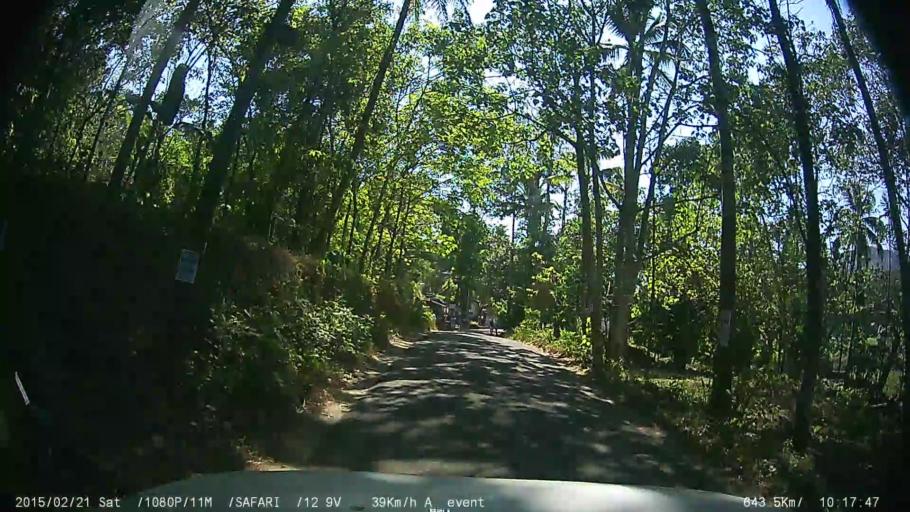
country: IN
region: Kerala
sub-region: Ernakulam
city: Muvattupuzha
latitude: 9.8766
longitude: 76.6492
